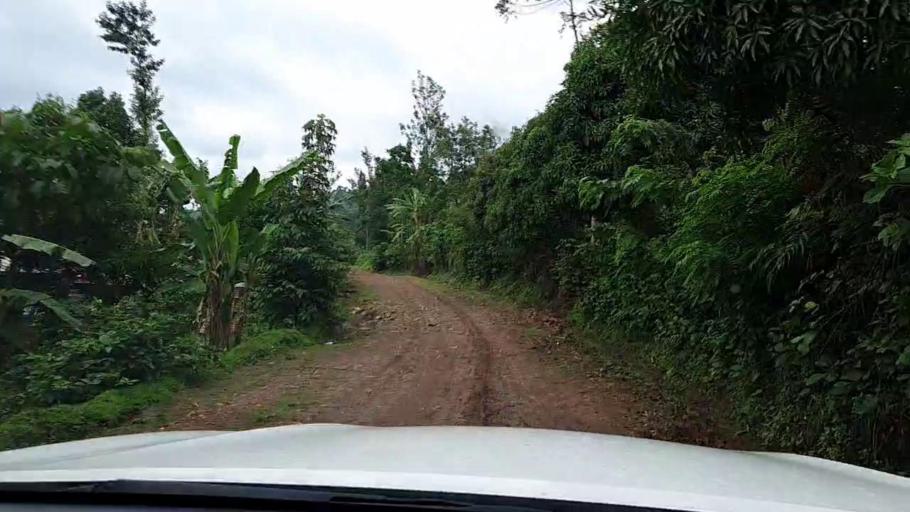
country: RW
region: Western Province
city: Cyangugu
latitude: -2.5522
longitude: 29.0369
